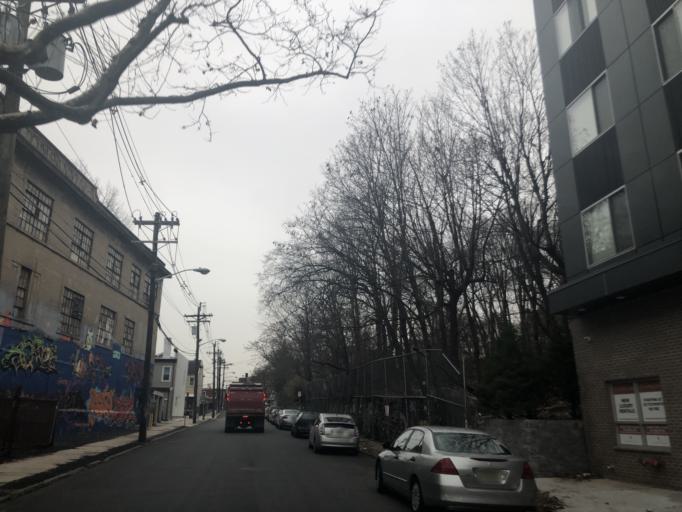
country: US
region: New Jersey
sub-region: Hudson County
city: Jersey City
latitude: 40.7176
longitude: -74.0663
